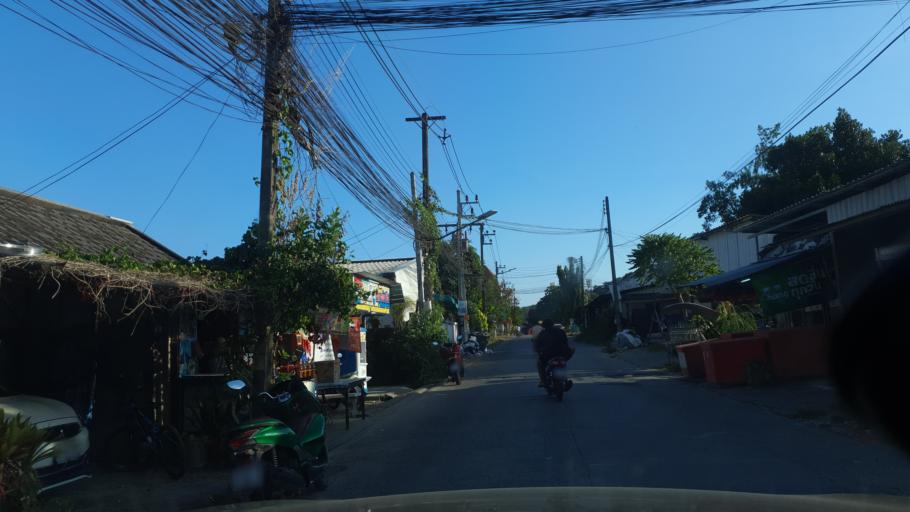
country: TH
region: Phuket
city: Kathu
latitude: 7.9046
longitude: 98.3296
